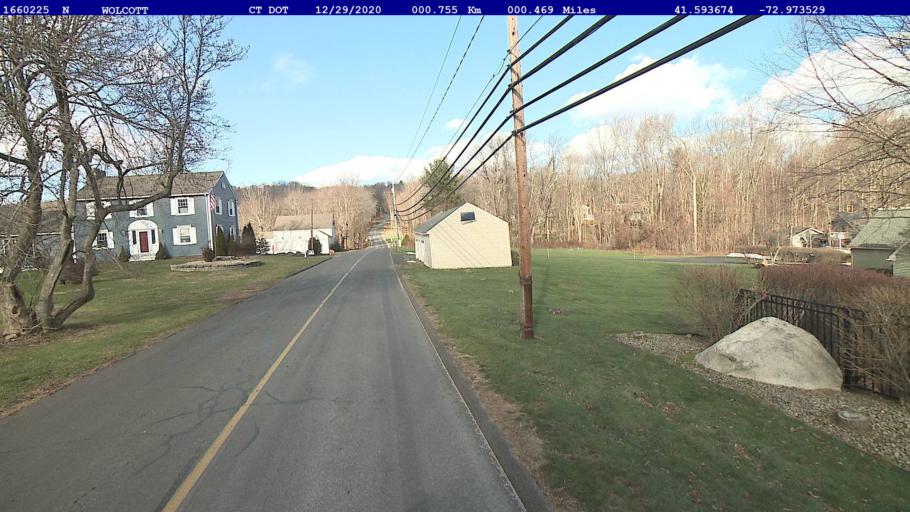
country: US
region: Connecticut
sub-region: New Haven County
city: Wolcott
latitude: 41.5937
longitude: -72.9735
